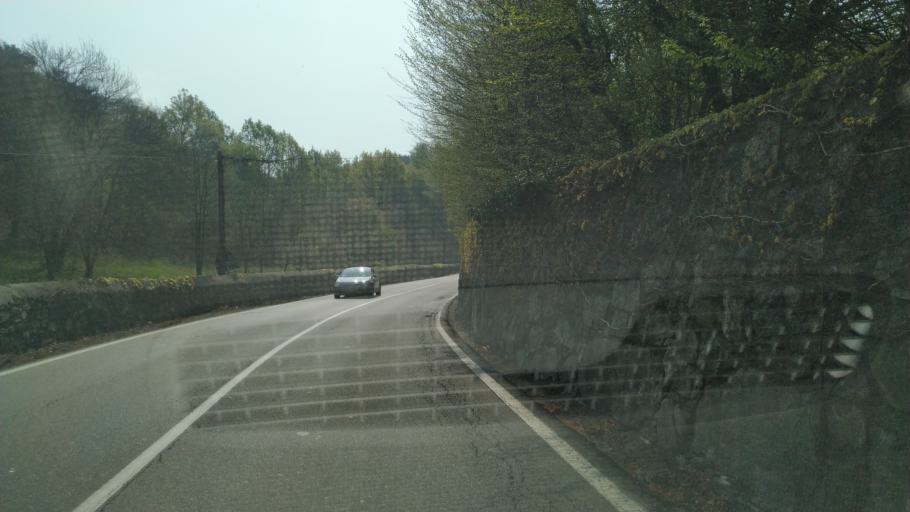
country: IT
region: Piedmont
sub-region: Provincia di Novara
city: Soriso
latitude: 45.7609
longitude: 8.4188
